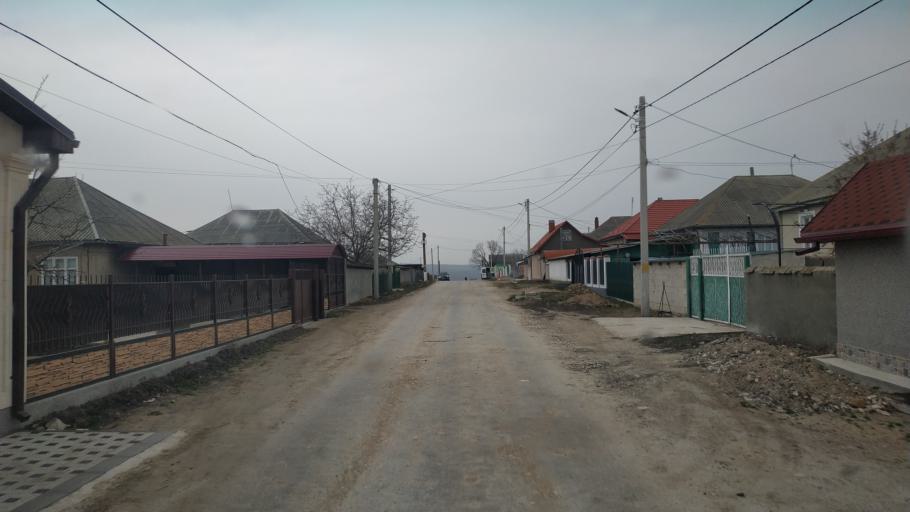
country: MD
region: Chisinau
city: Singera
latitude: 46.8247
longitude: 28.9639
